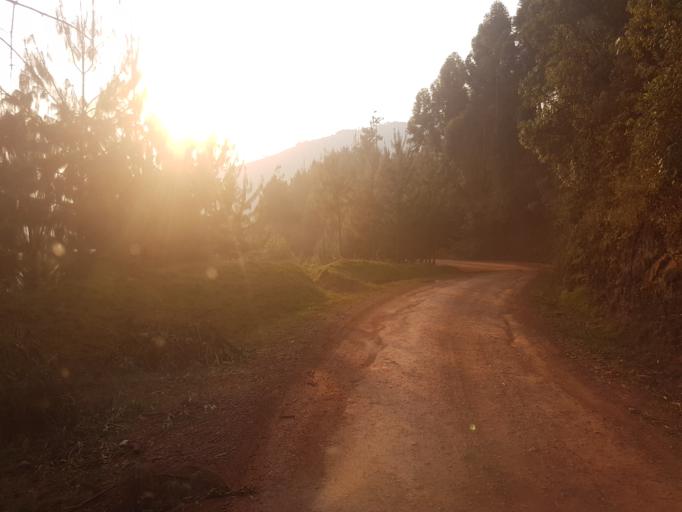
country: UG
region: Western Region
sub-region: Kanungu District
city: Kanungu
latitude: -1.0078
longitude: 29.8467
